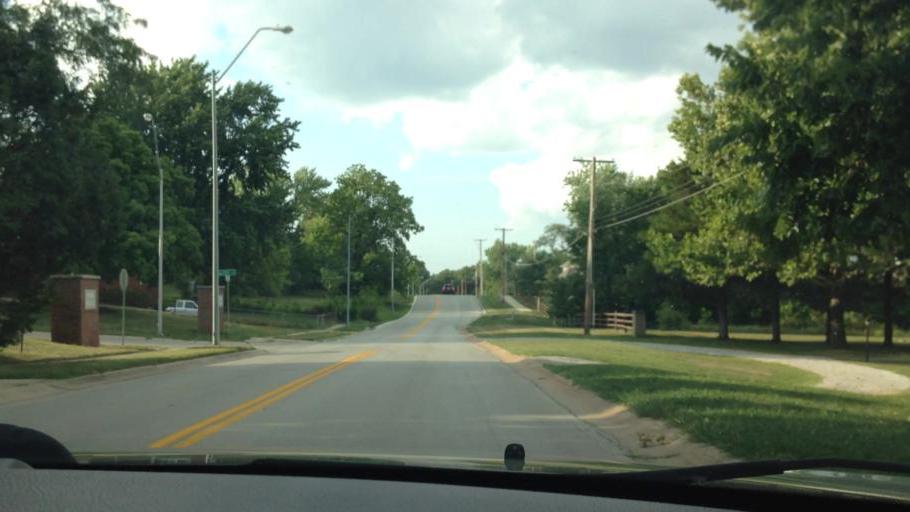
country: US
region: Missouri
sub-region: Platte County
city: Parkville
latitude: 39.2210
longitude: -94.6404
